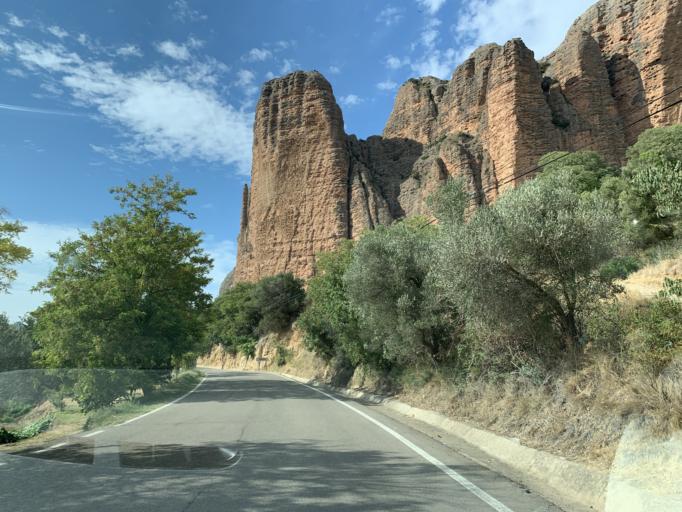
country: ES
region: Aragon
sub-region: Provincia de Zaragoza
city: Santa Eulalia de Gallego
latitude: 42.3463
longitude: -0.7262
